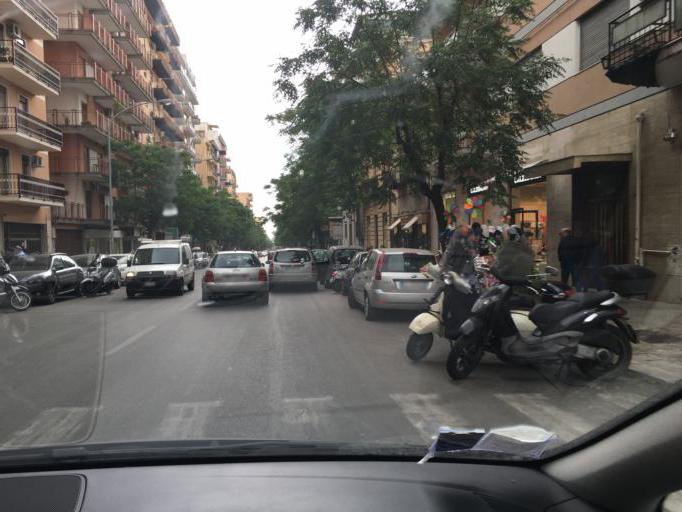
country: IT
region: Sicily
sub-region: Palermo
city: Palermo
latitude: 38.1049
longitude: 13.3349
